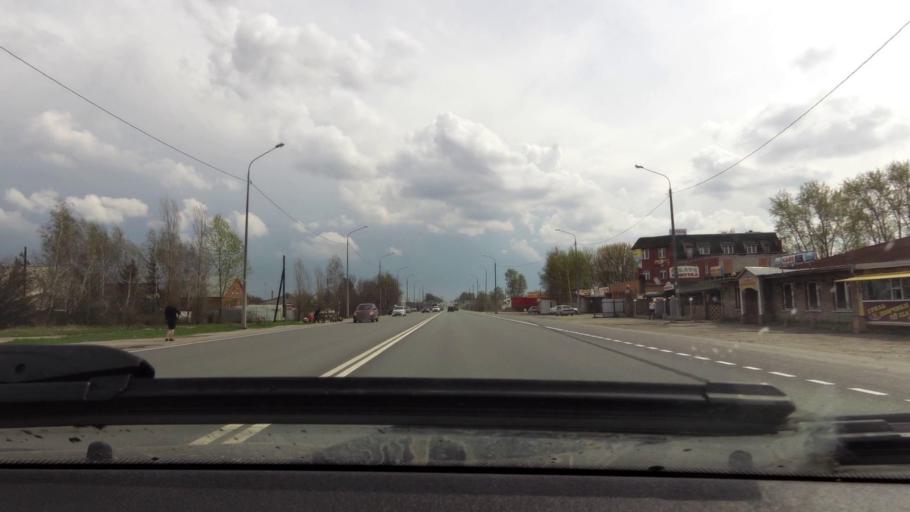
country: RU
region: Rjazan
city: Bagramovo
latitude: 54.7326
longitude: 39.4595
